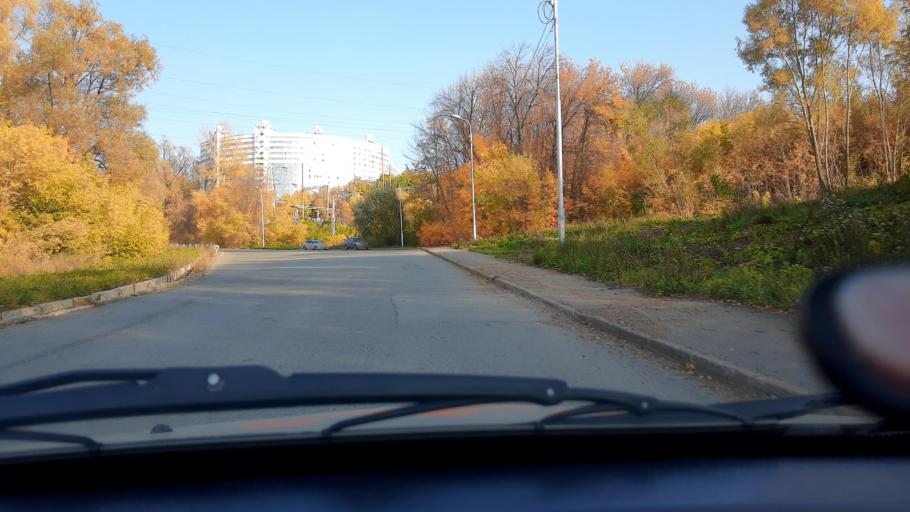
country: RU
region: Bashkortostan
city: Ufa
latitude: 54.8122
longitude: 56.0508
